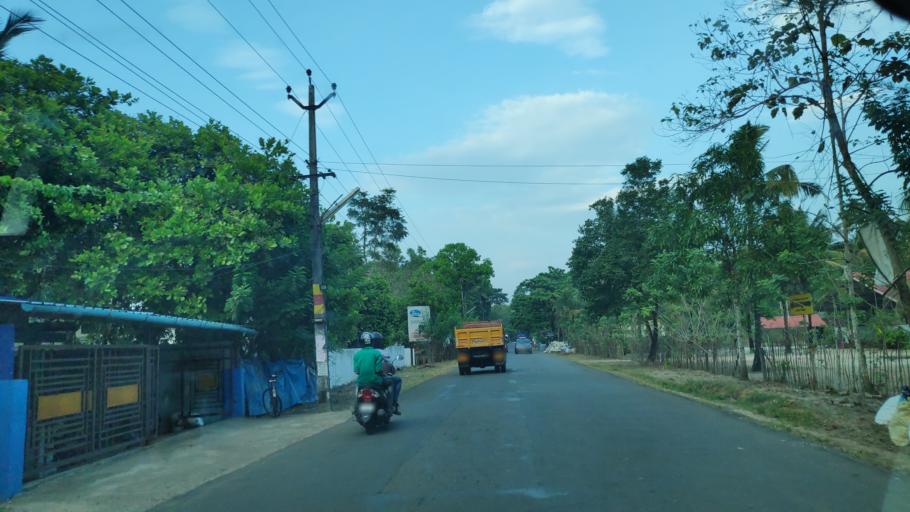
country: IN
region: Kerala
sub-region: Alappuzha
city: Shertallai
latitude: 9.6565
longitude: 76.3759
